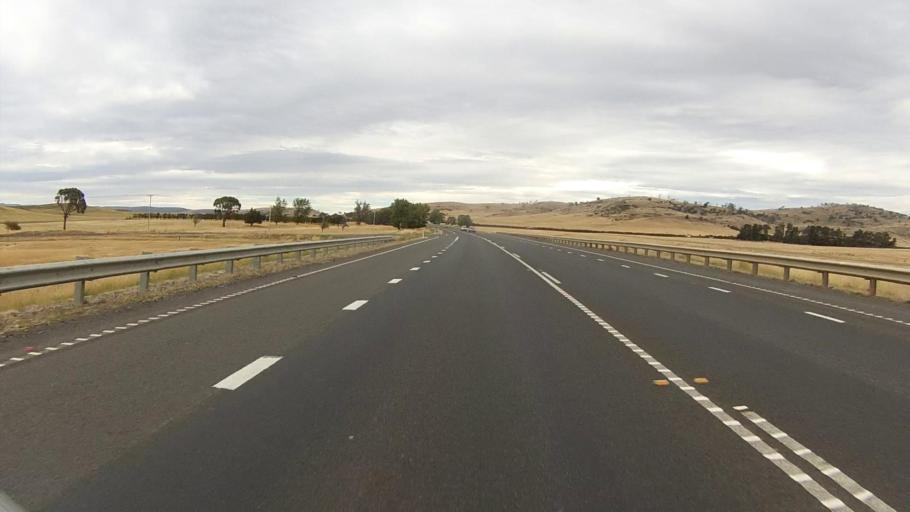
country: AU
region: Tasmania
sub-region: Brighton
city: Bridgewater
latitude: -42.3704
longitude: 147.3331
